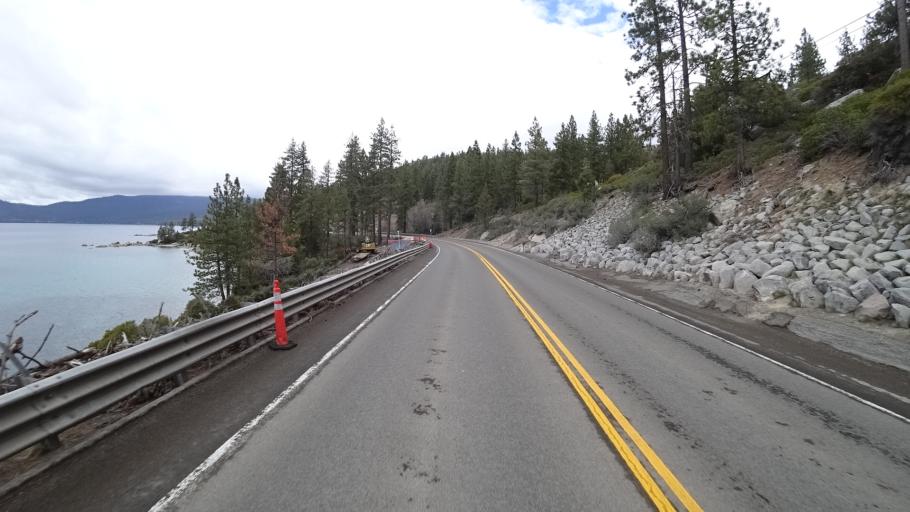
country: US
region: Nevada
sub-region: Washoe County
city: Incline Village
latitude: 39.2203
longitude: -119.9274
